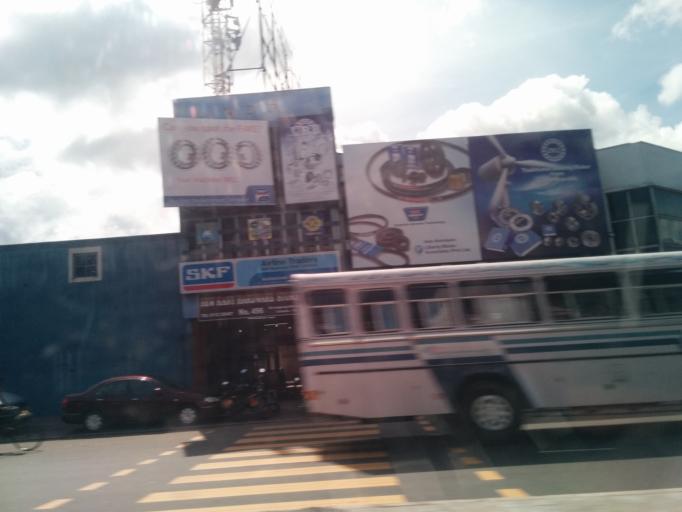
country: LK
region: Western
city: Kolonnawa
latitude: 6.9385
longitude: 79.8664
